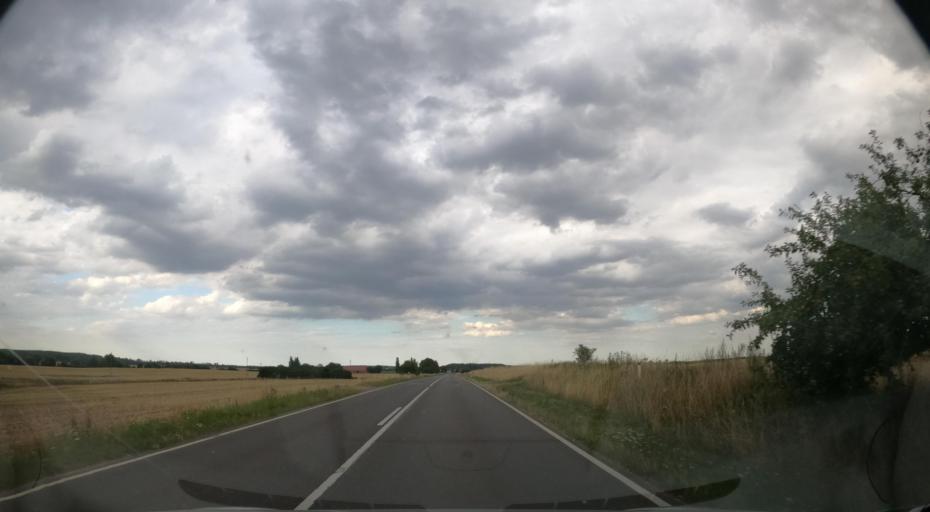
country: DE
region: Mecklenburg-Vorpommern
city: Woldegk
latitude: 53.4644
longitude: 13.6167
